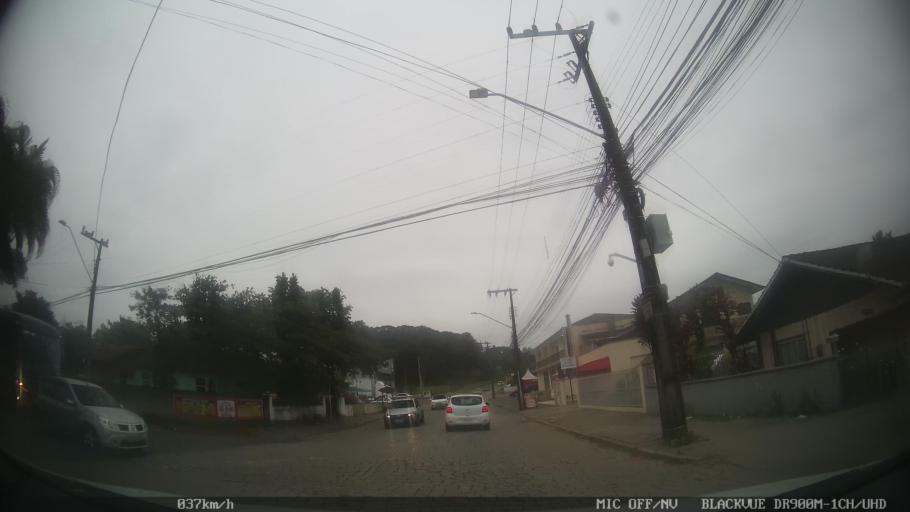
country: BR
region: Santa Catarina
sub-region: Joinville
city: Joinville
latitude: -26.3330
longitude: -48.8579
